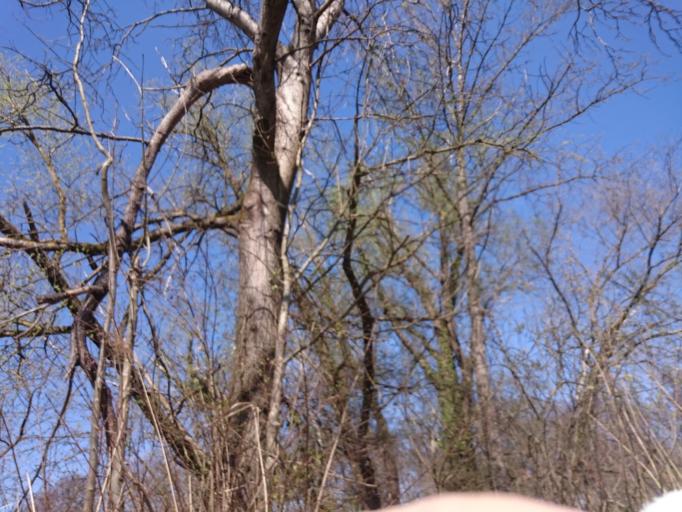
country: DE
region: Rheinland-Pfalz
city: Neupotz
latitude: 49.0790
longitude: 8.3063
